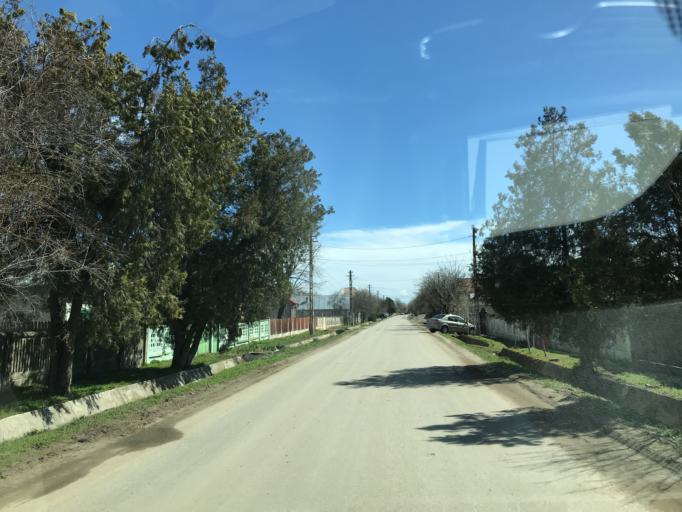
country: RO
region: Olt
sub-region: Comuna Osica de Sus
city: Osica de Sus
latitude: 44.2543
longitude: 24.3159
